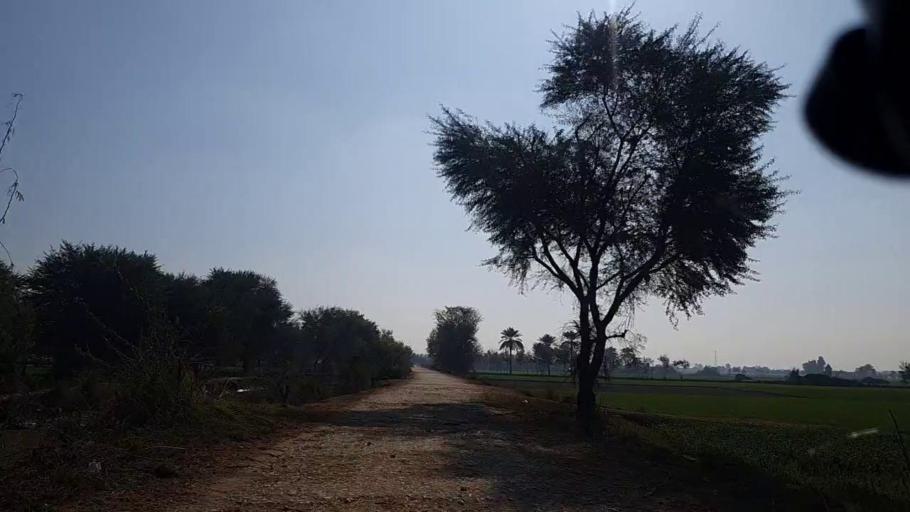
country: PK
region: Sindh
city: Khanpur
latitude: 27.7795
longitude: 69.4228
